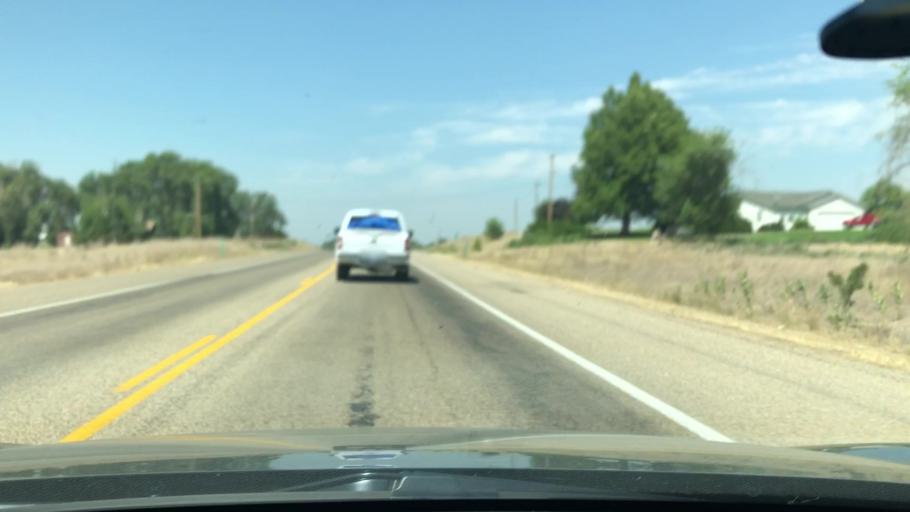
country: US
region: Idaho
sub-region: Canyon County
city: Parma
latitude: 43.8352
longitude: -116.9545
